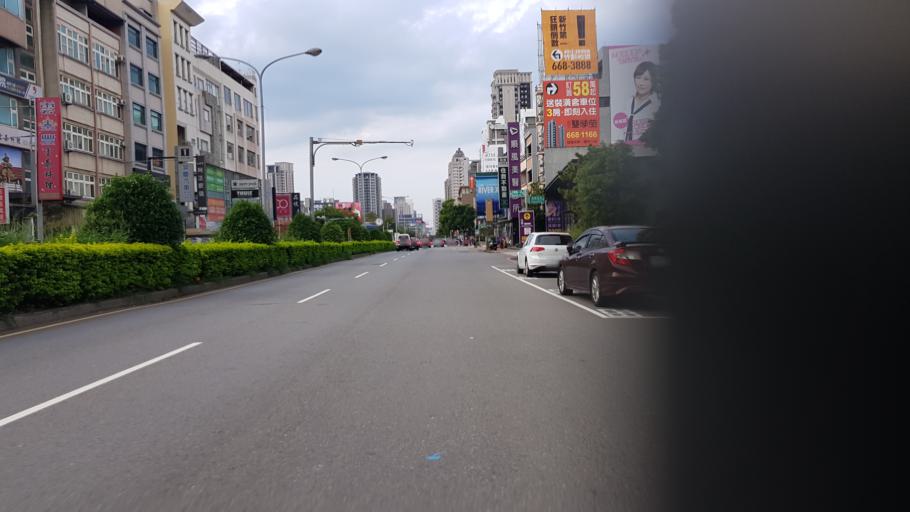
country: TW
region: Taiwan
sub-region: Hsinchu
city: Zhubei
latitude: 24.8124
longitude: 121.0252
